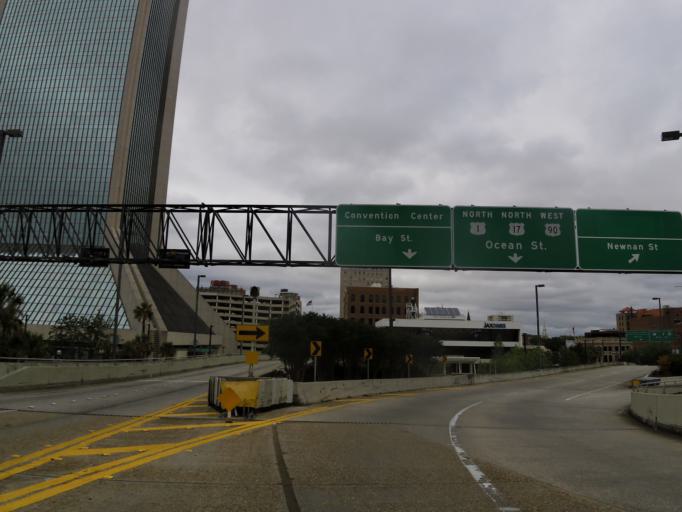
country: US
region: Florida
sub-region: Duval County
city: Jacksonville
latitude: 30.3236
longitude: -81.6565
